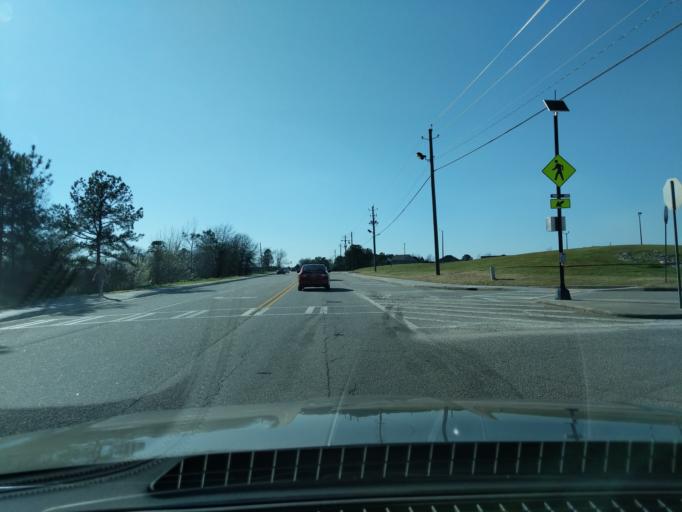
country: US
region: Georgia
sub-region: Columbia County
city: Grovetown
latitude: 33.4520
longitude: -82.2194
